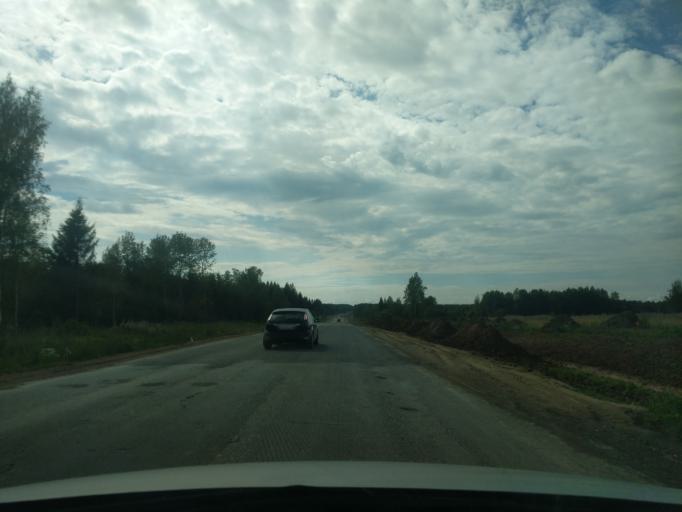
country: RU
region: Kostroma
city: Sudislavl'
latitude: 57.8573
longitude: 41.6084
